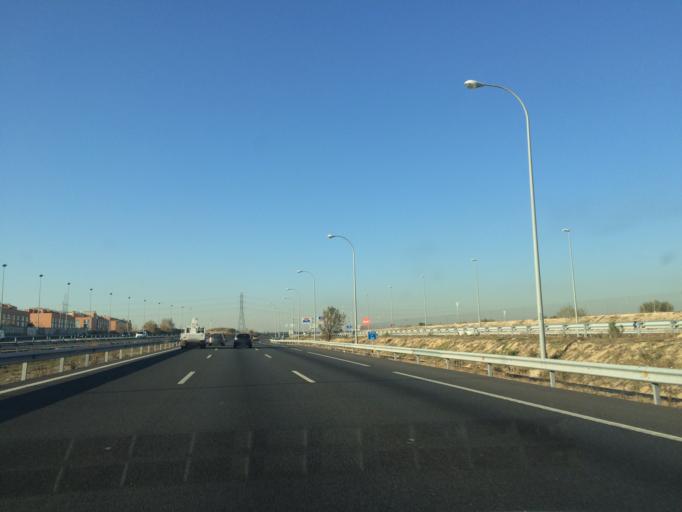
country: ES
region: Madrid
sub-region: Provincia de Madrid
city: Pozuelo de Alarcon
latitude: 40.3914
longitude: -3.8305
